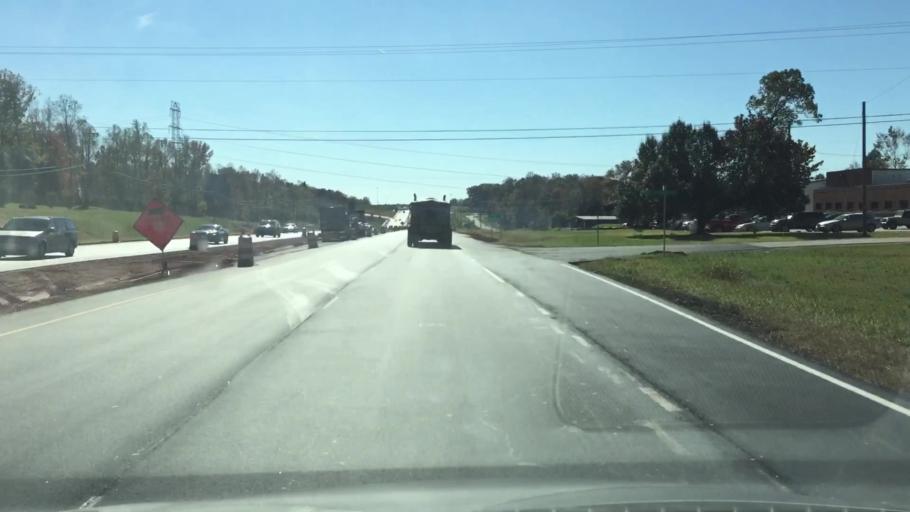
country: US
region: North Carolina
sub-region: Guilford County
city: McLeansville
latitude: 36.1624
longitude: -79.7214
